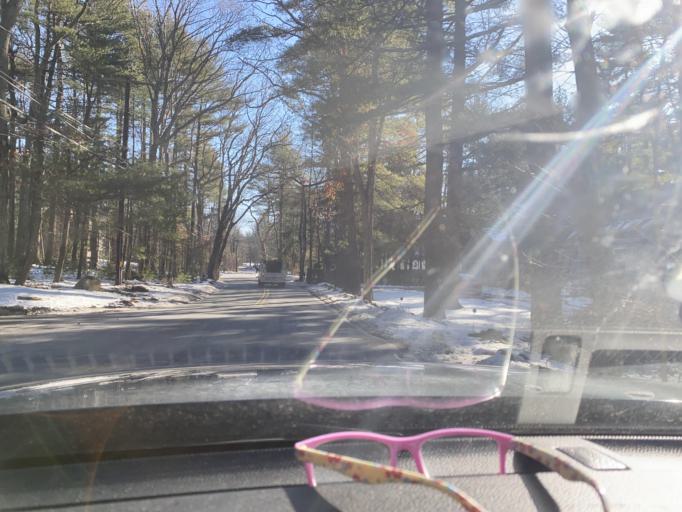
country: US
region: Massachusetts
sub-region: Norfolk County
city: Walpole
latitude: 42.1652
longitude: -71.2607
